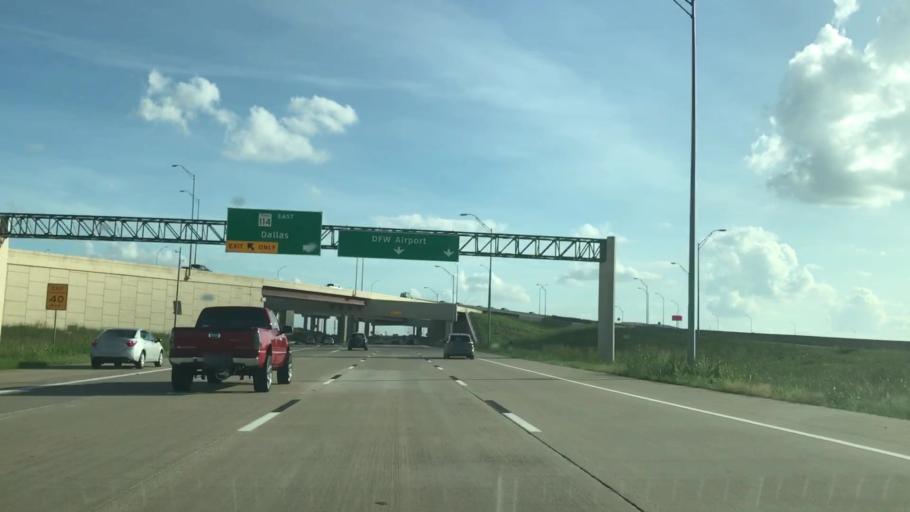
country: US
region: Texas
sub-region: Dallas County
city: Coppell
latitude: 32.9376
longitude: -97.0414
